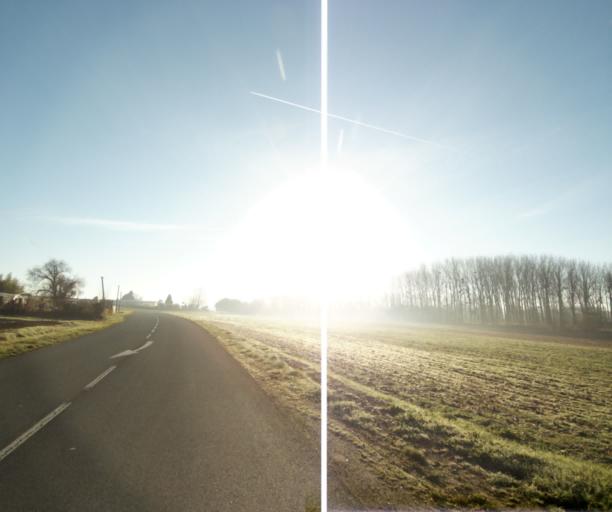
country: FR
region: Poitou-Charentes
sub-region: Departement de la Charente-Maritime
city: Cherac
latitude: 45.6966
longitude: -0.4818
